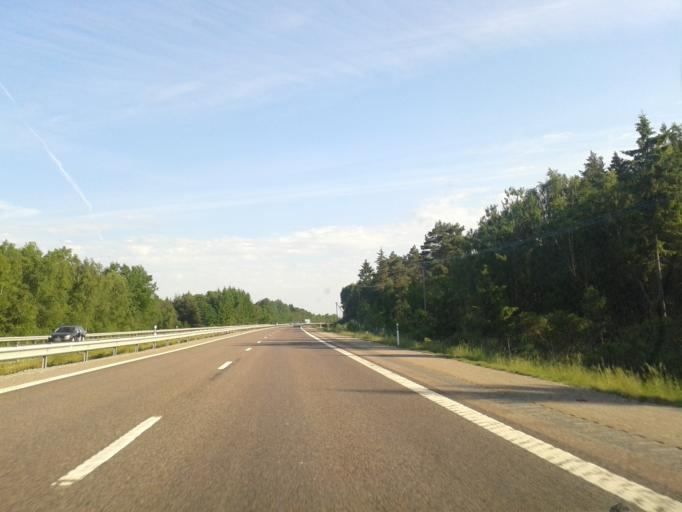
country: SE
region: Vaestra Goetaland
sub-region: Kungalvs Kommun
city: Kode
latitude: 57.9655
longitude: 11.8424
